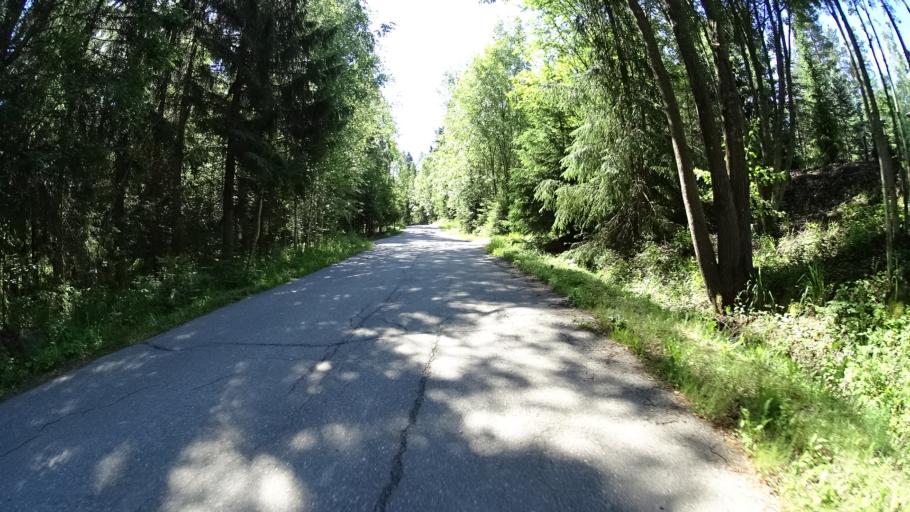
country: FI
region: Uusimaa
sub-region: Helsinki
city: Vihti
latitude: 60.3035
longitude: 24.4430
